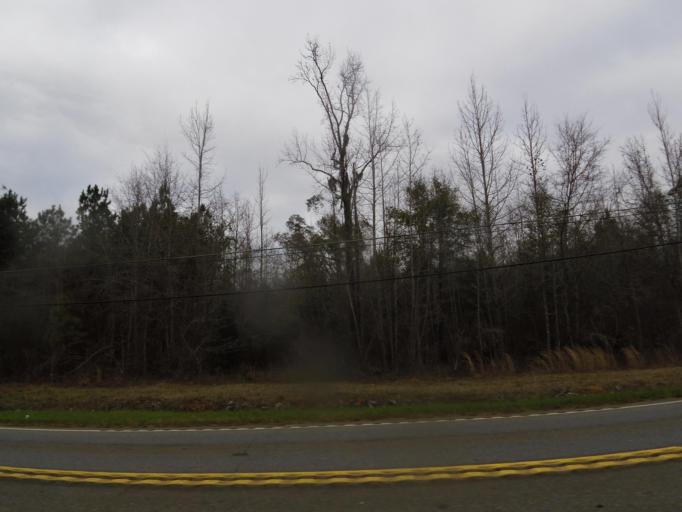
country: US
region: Georgia
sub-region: Randolph County
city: Cuthbert
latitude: 31.7700
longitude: -84.7735
